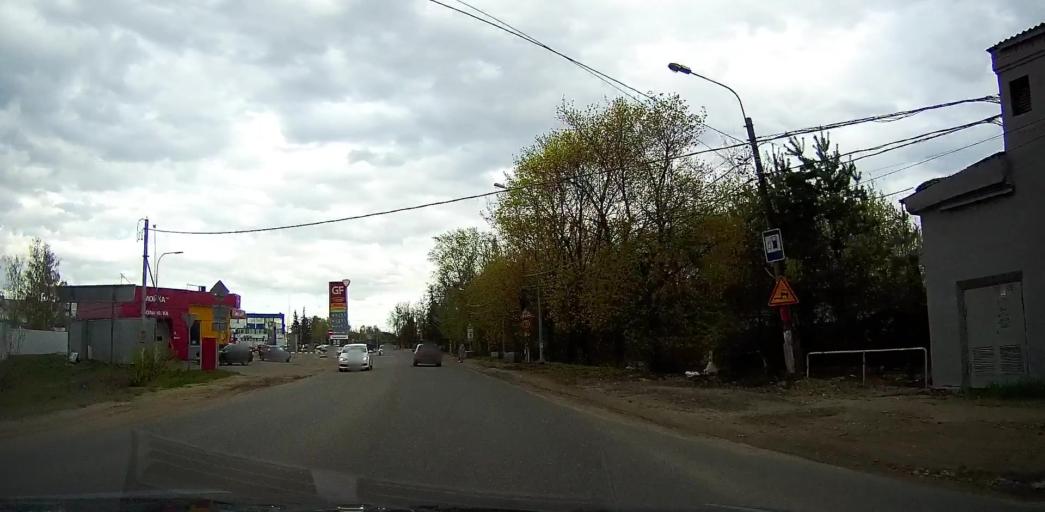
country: RU
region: Moskovskaya
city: Pavlovskiy Posad
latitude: 55.7731
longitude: 38.6866
